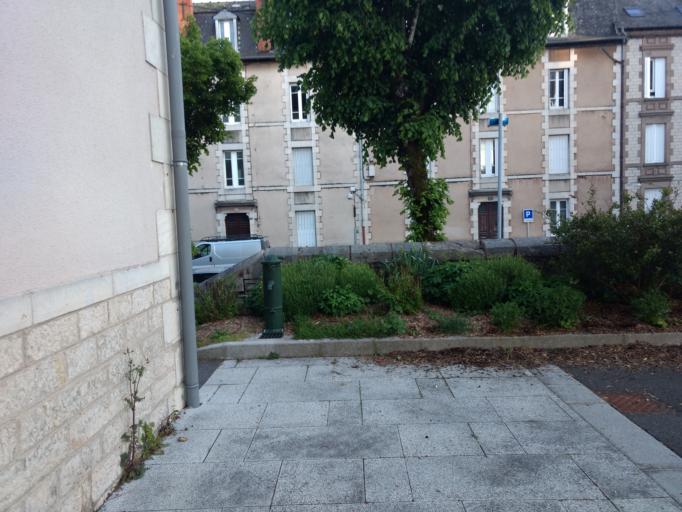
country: FR
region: Midi-Pyrenees
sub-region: Departement de l'Aveyron
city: Rodez
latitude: 44.3565
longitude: 2.5785
